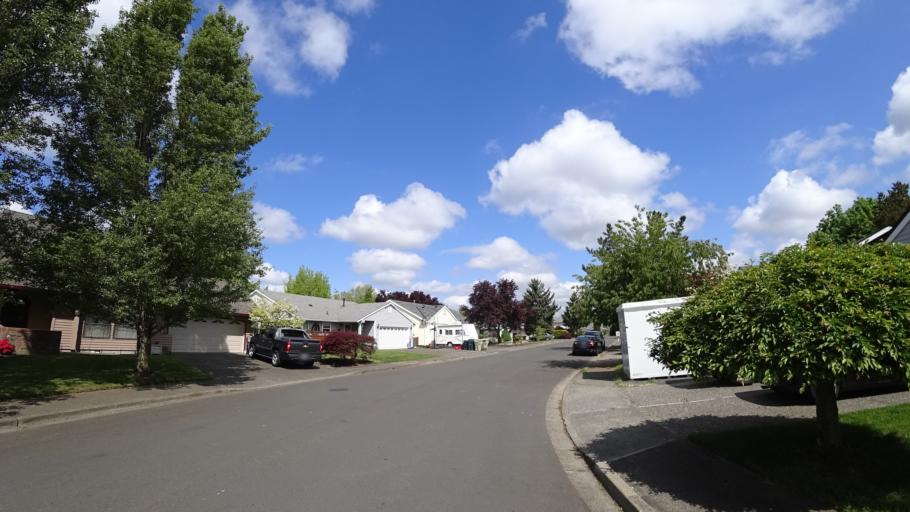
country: US
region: Oregon
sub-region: Washington County
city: Aloha
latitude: 45.5080
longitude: -122.8919
